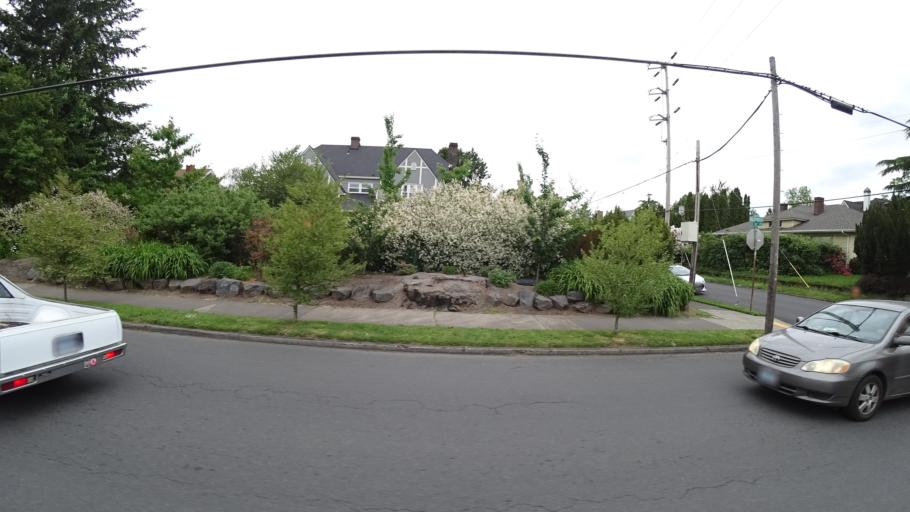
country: US
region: Oregon
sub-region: Multnomah County
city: Lents
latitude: 45.5192
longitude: -122.6123
